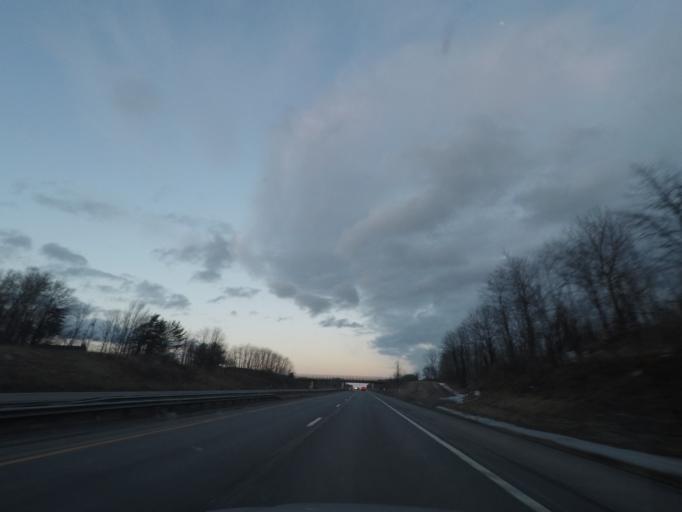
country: US
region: New York
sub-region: Montgomery County
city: Tribes Hill
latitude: 42.9317
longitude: -74.2738
